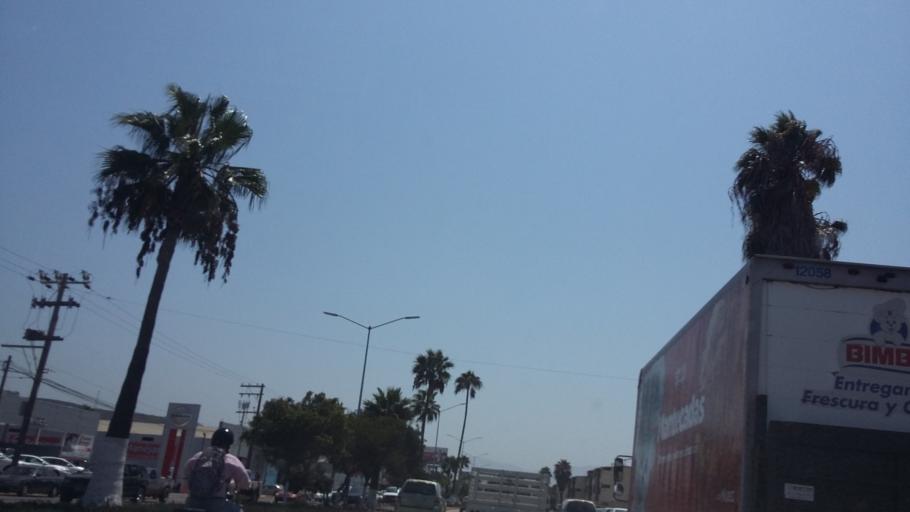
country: MX
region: Baja California
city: Ensenada
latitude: 31.8326
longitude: -116.6012
